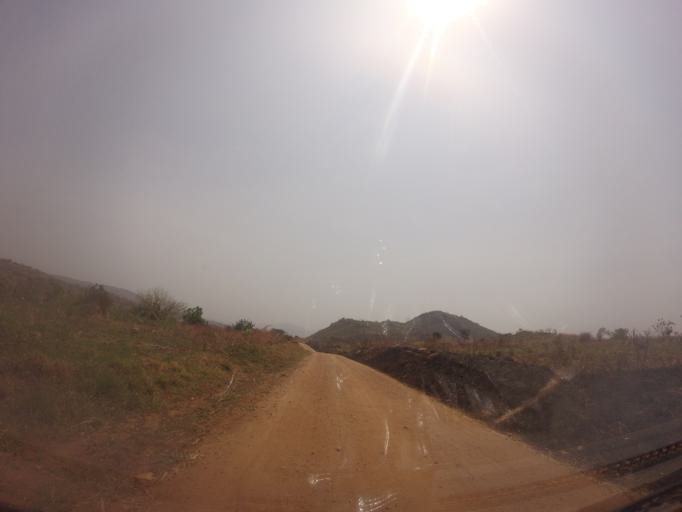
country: UG
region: Northern Region
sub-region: Arua District
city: Arua
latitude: 2.9256
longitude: 30.9833
